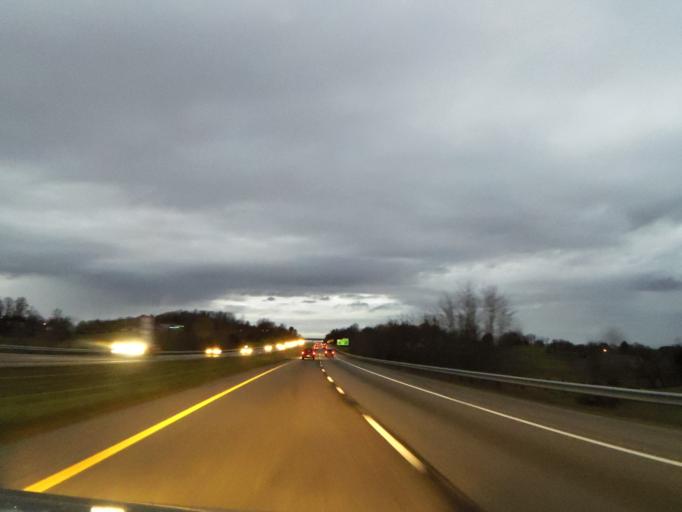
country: US
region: Tennessee
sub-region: Washington County
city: Gray
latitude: 36.3955
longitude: -82.4581
